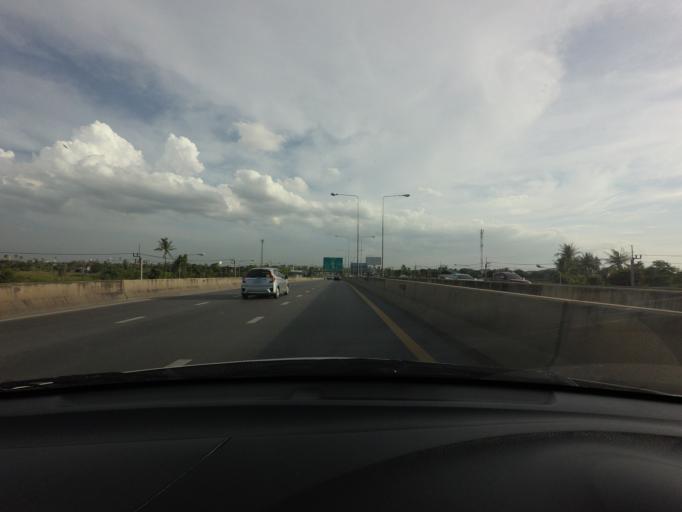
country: TH
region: Nonthaburi
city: Bang Bua Thong
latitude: 13.9401
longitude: 100.4579
